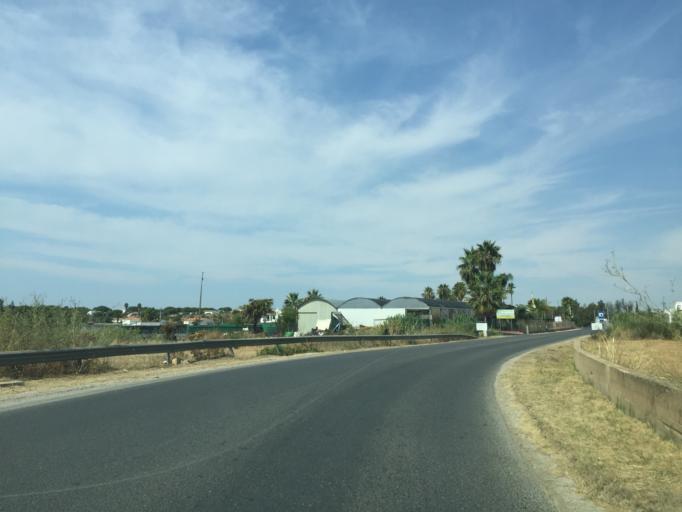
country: PT
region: Faro
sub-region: Loule
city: Quarteira
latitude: 37.0725
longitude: -8.0692
